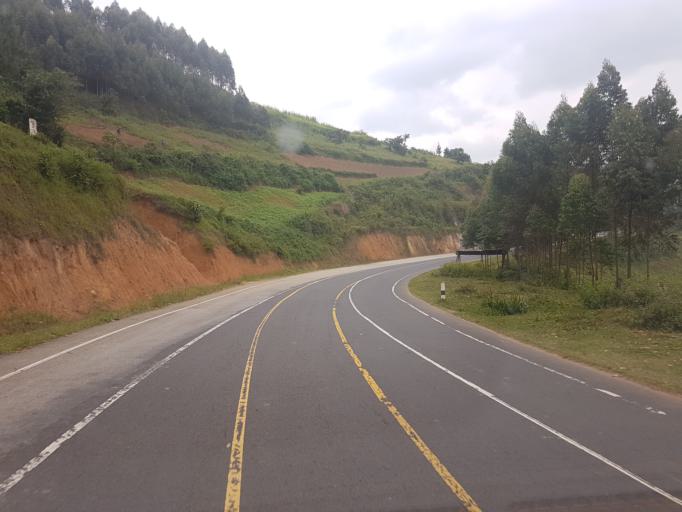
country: UG
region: Western Region
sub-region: Kabale District
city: Kabale
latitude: -1.2070
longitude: 29.8333
